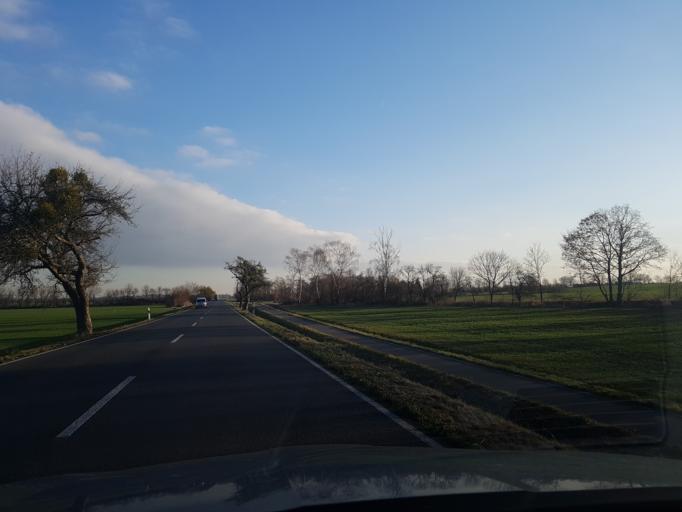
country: DE
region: Brandenburg
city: Luckau
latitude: 51.8349
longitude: 13.6495
